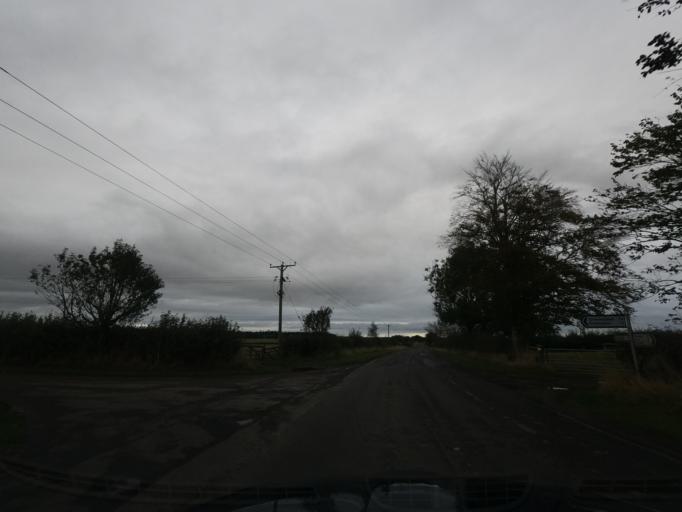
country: GB
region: England
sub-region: Northumberland
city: Ford
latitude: 55.6912
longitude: -2.0802
